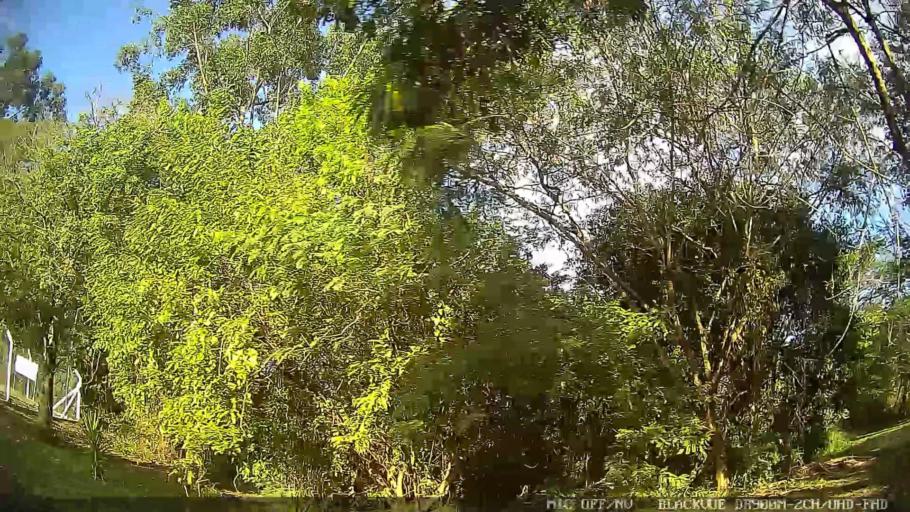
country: BR
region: Sao Paulo
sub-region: Salto
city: Salto
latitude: -23.1922
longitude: -47.2643
